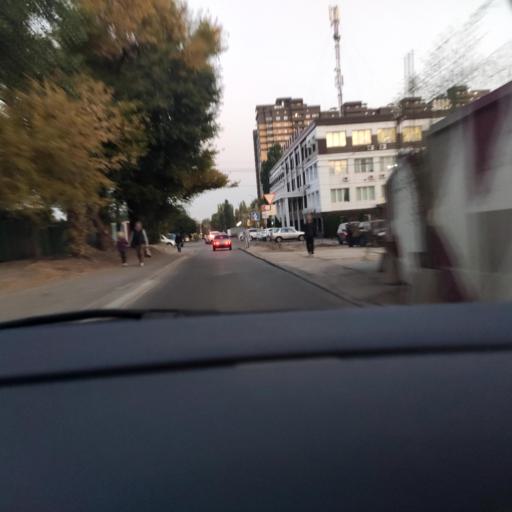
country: RU
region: Voronezj
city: Voronezh
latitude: 51.6422
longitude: 39.1501
